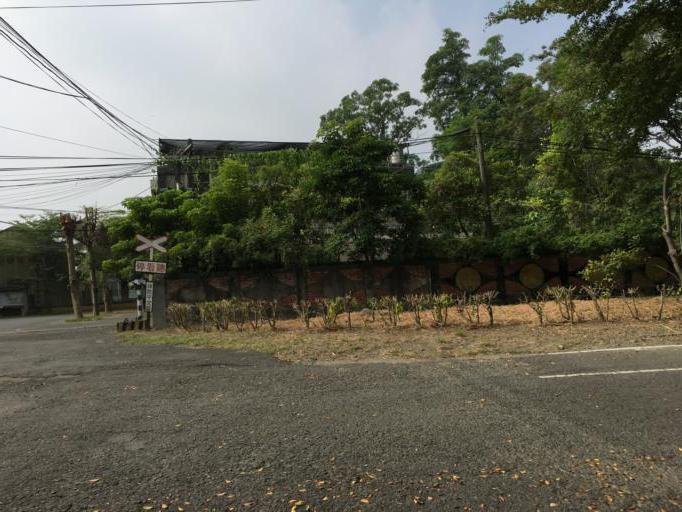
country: TW
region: Taiwan
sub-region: Chiayi
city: Taibao
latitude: 23.4804
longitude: 120.2977
